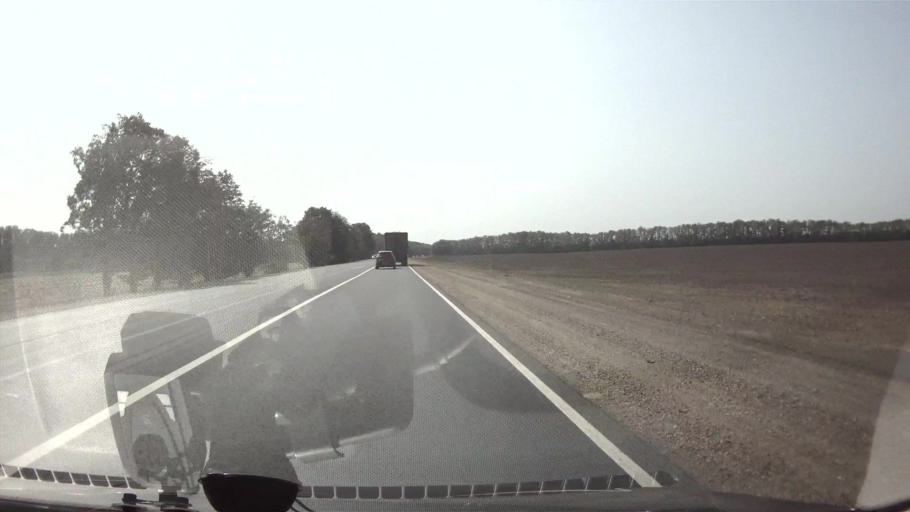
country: RU
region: Adygeya
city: Krasnogvardeyskoye
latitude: 45.2026
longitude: 39.5366
